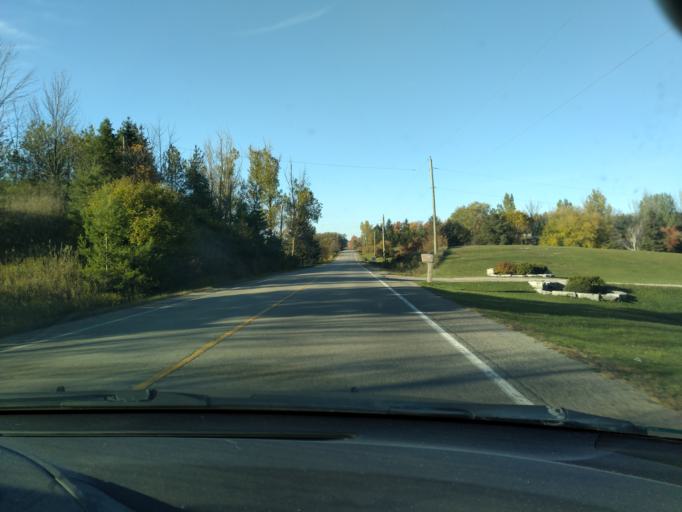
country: CA
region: Ontario
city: Bradford West Gwillimbury
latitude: 43.9486
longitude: -79.7149
